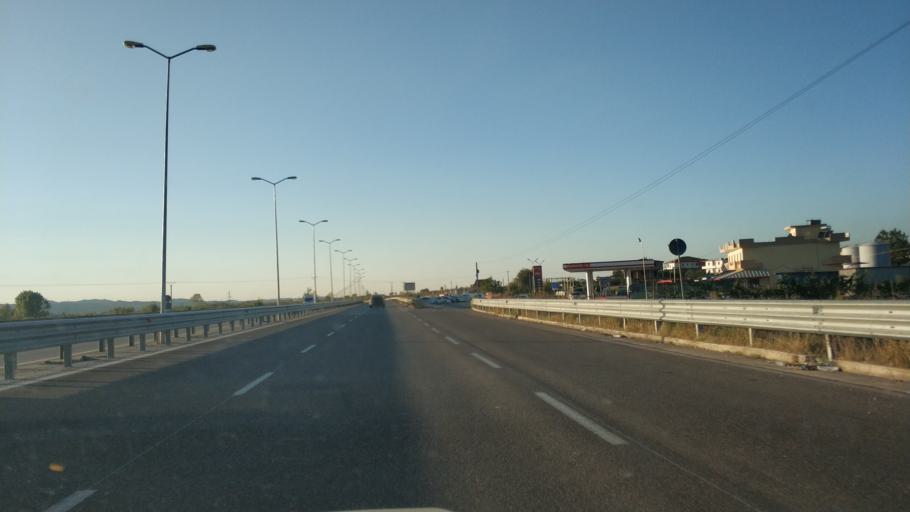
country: AL
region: Tirane
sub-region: Rrethi i Kavajes
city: Gose e Madhe
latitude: 41.0827
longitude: 19.6203
